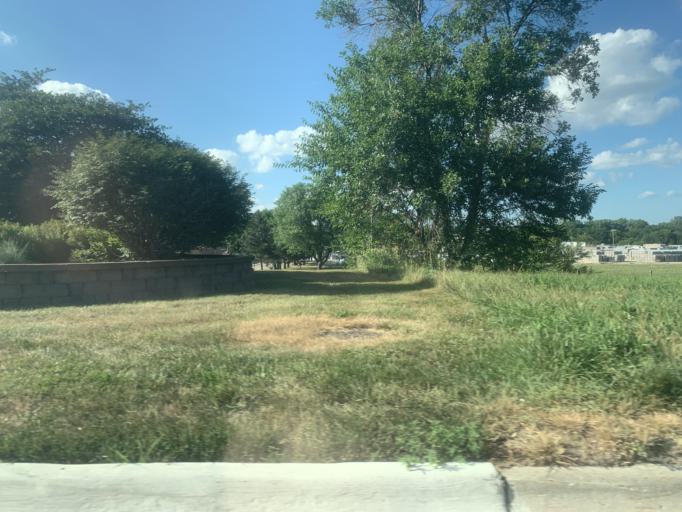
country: US
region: Nebraska
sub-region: Sarpy County
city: Chalco
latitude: 41.1764
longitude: -96.1371
